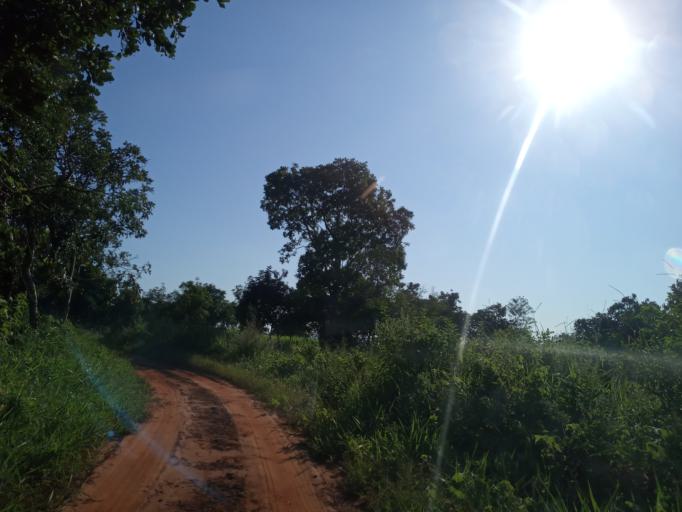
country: BR
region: Minas Gerais
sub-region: Ituiutaba
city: Ituiutaba
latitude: -18.9757
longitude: -49.4981
